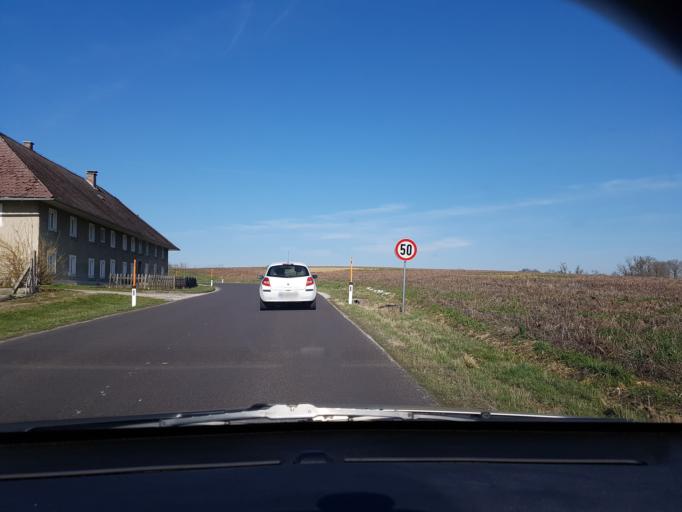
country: AT
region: Upper Austria
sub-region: Politischer Bezirk Linz-Land
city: Ansfelden
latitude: 48.2034
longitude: 14.3085
